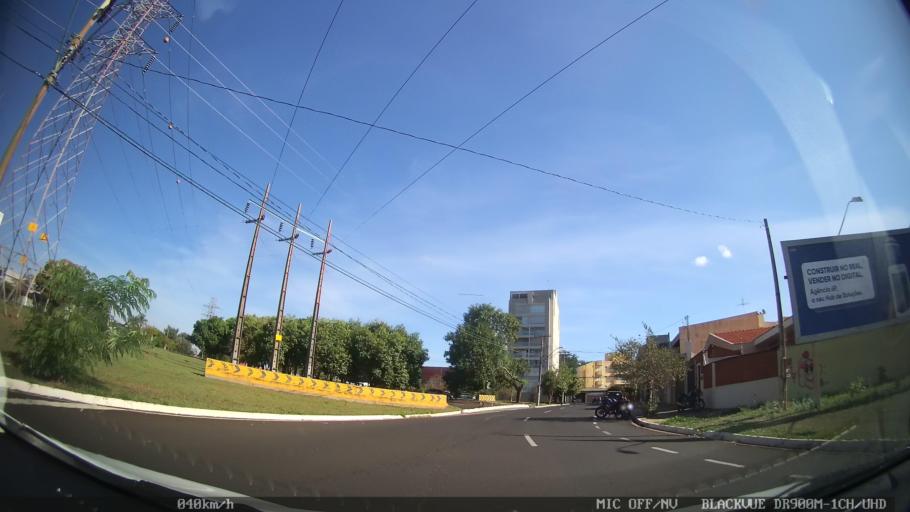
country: BR
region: Sao Paulo
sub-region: Ribeirao Preto
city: Ribeirao Preto
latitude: -21.1850
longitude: -47.7836
